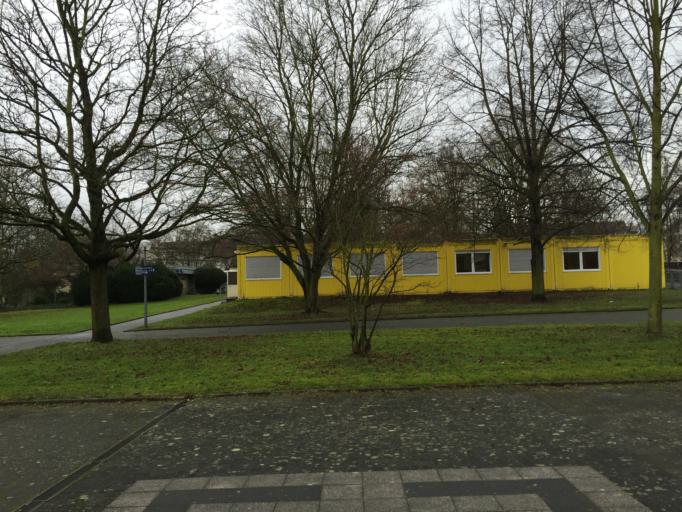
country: DE
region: North Rhine-Westphalia
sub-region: Regierungsbezirk Koln
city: Bonn
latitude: 50.7520
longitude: 7.0974
